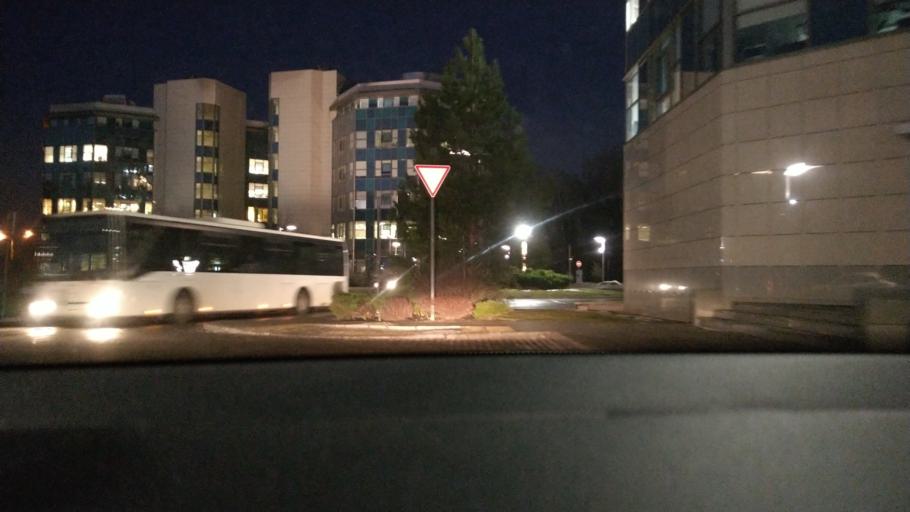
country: RU
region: Moscow
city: Khimki
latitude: 55.9476
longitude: 37.4192
